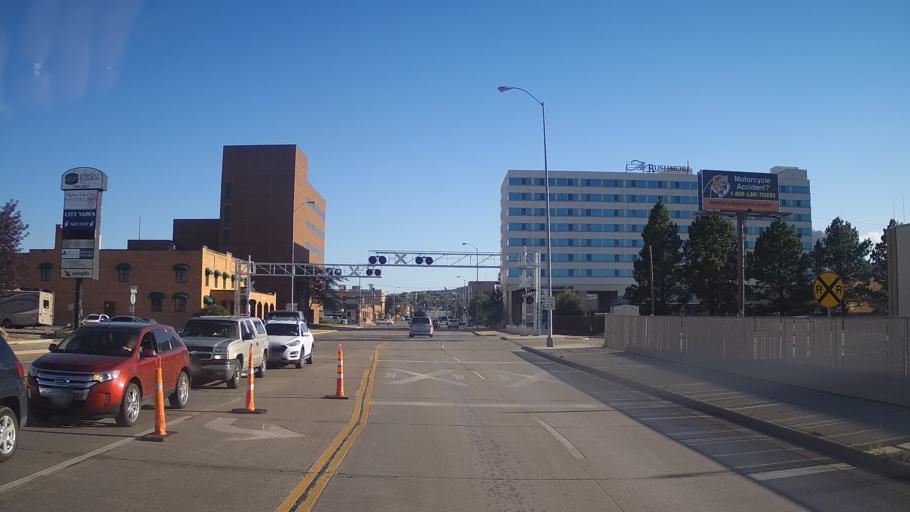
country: US
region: South Dakota
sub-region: Pennington County
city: Rapid City
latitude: 44.0834
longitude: -103.2302
